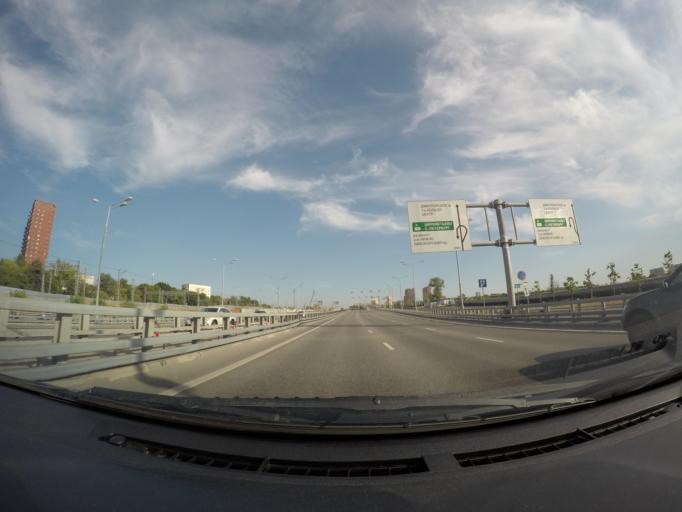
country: RU
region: Moscow
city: Likhobory
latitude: 55.8431
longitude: 37.5616
